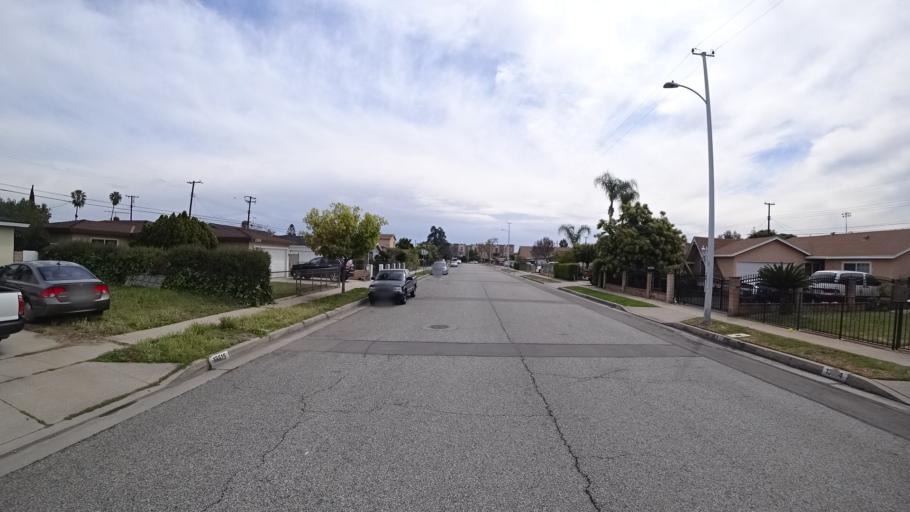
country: US
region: California
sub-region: Los Angeles County
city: Baldwin Park
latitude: 34.0770
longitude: -117.9772
